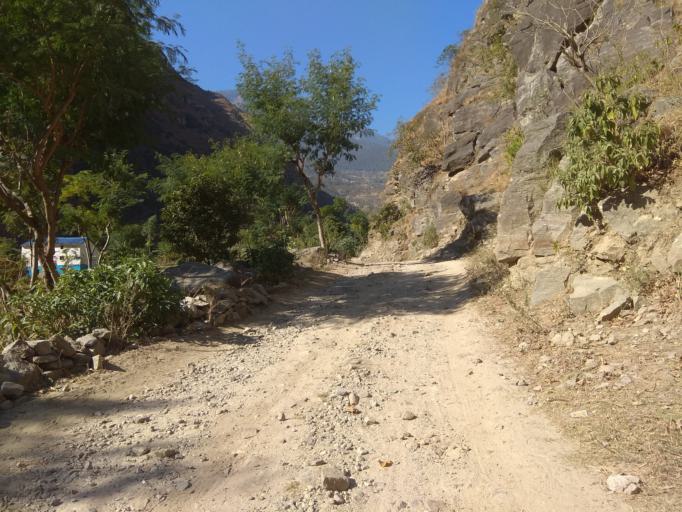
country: NP
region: Far Western
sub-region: Seti Zone
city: Achham
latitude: 29.2192
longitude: 81.6335
